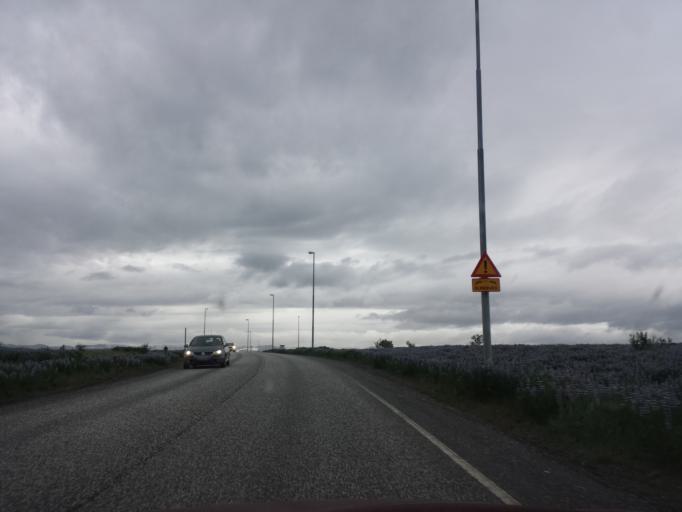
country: IS
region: Capital Region
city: Alftanes
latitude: 64.0897
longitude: -21.9845
